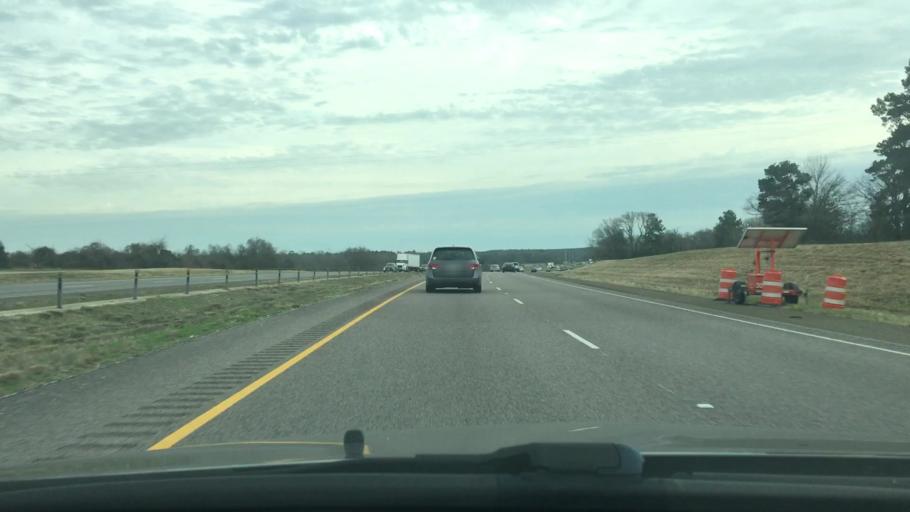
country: US
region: Texas
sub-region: Madison County
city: Madisonville
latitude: 30.9090
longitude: -95.7896
